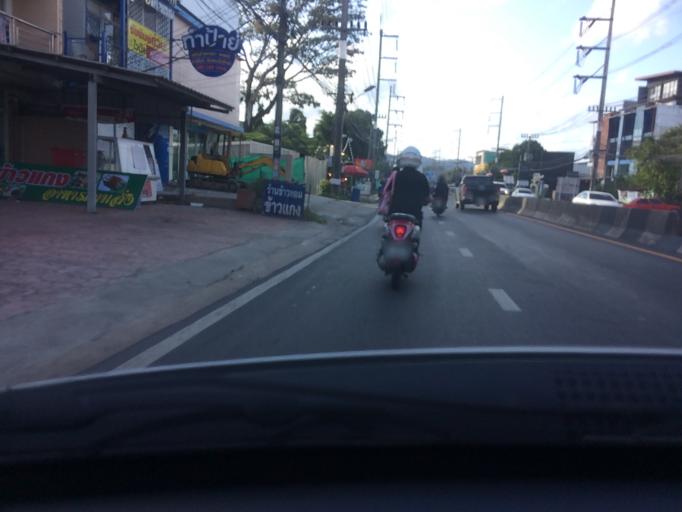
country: TH
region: Phuket
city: Mueang Phuket
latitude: 7.8778
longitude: 98.3636
